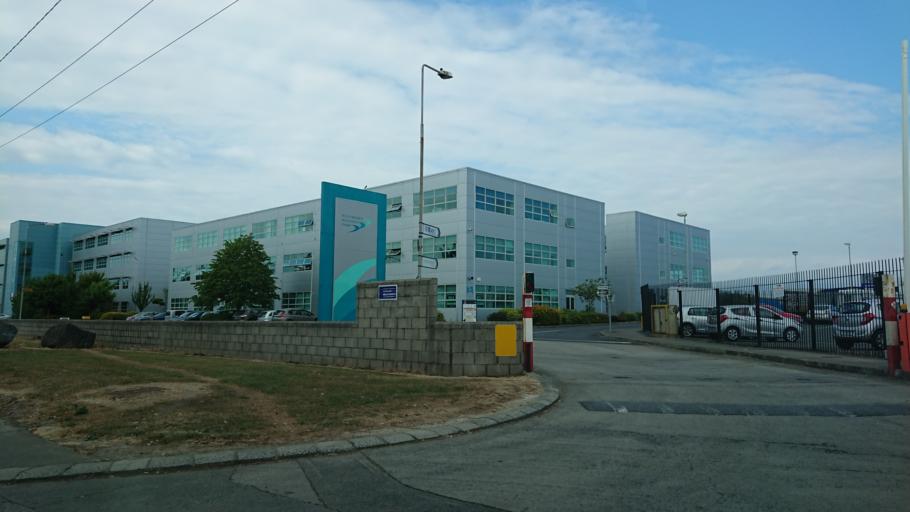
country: IE
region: Munster
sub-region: Waterford
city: Waterford
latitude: 52.2438
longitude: -7.1595
